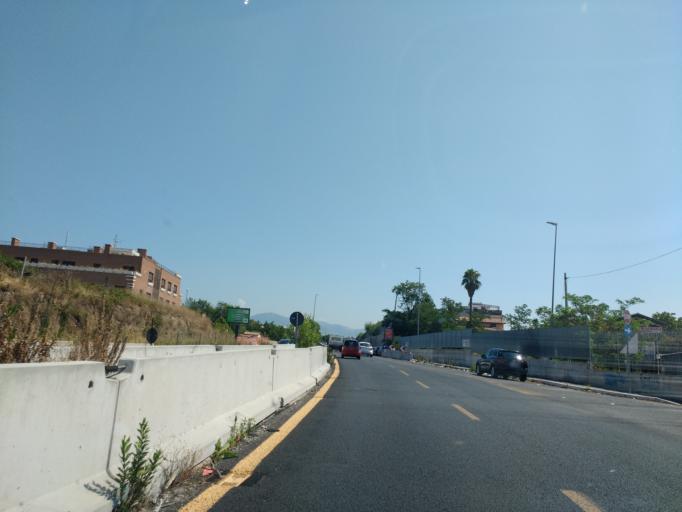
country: IT
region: Latium
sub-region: Citta metropolitana di Roma Capitale
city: Setteville
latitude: 41.9390
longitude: 12.6288
